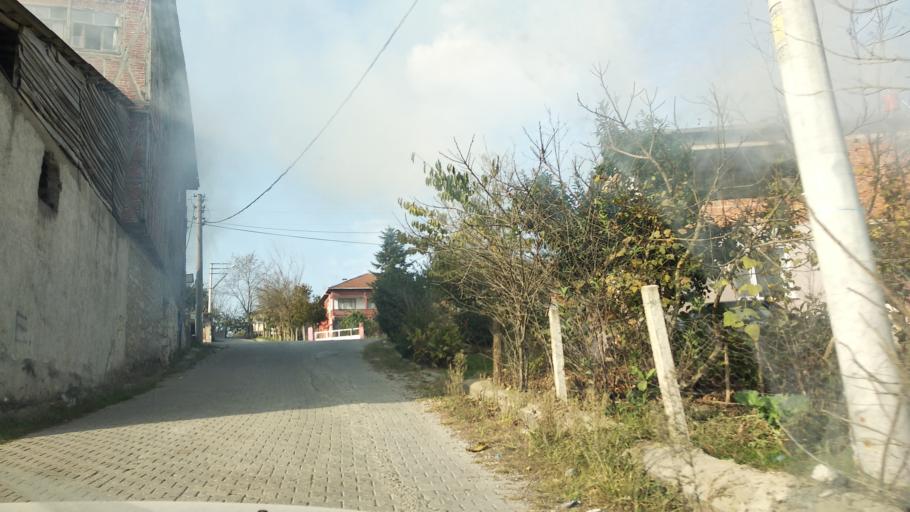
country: TR
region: Sakarya
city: Karasu
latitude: 41.0556
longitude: 30.6280
